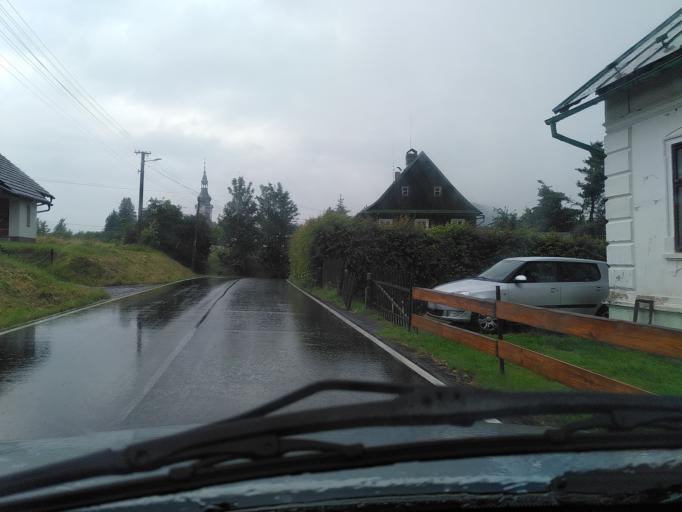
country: CZ
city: Novy Bor
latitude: 50.8099
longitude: 14.5375
